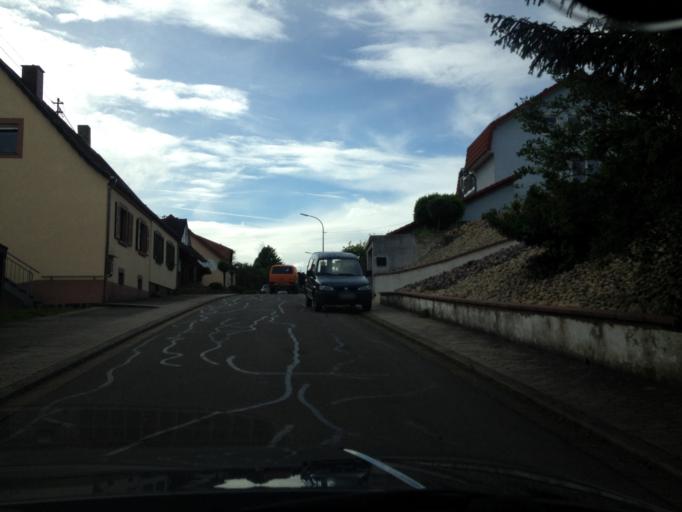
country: DE
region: Saarland
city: Marpingen
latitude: 49.4756
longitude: 7.0676
